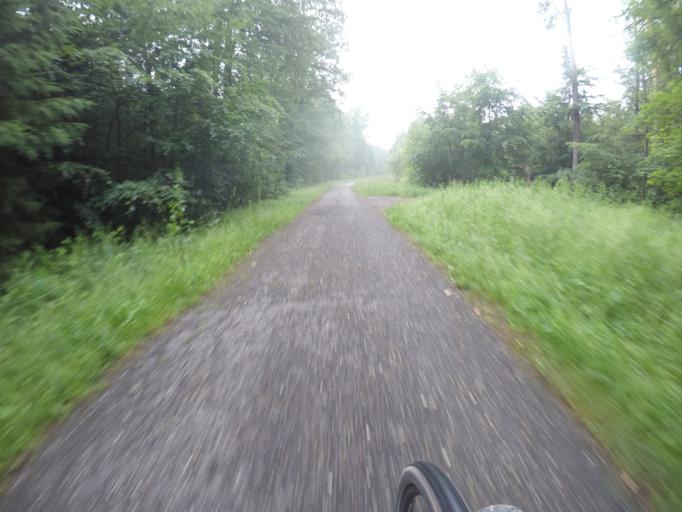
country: DE
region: Baden-Wuerttemberg
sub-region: Regierungsbezirk Stuttgart
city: Sindelfingen
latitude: 48.7215
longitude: 9.0535
